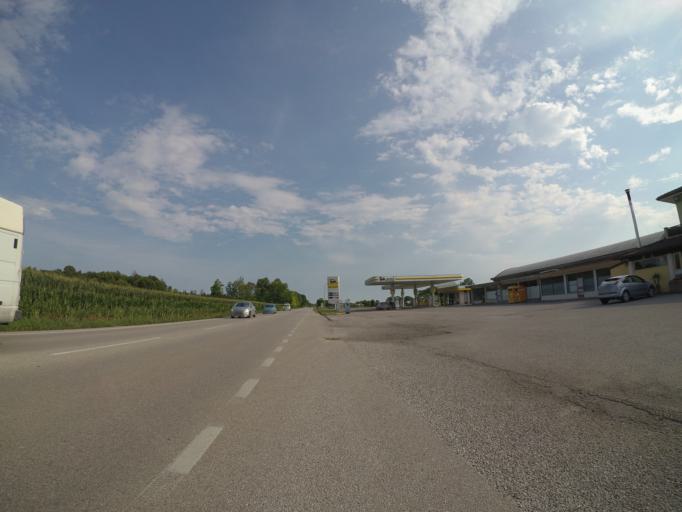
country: IT
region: Friuli Venezia Giulia
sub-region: Provincia di Udine
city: Codroipo
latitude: 45.9466
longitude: 12.9767
